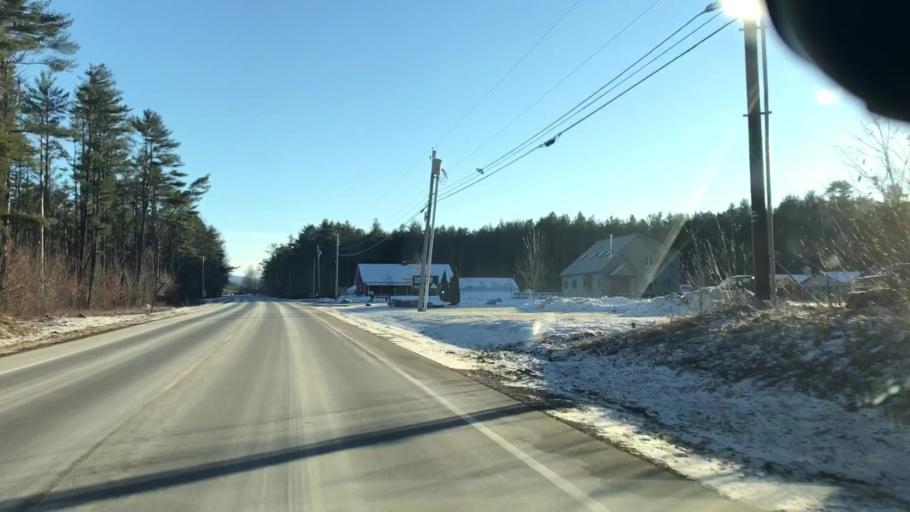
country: US
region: New Hampshire
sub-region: Grafton County
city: Orford
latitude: 43.8738
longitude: -72.1560
